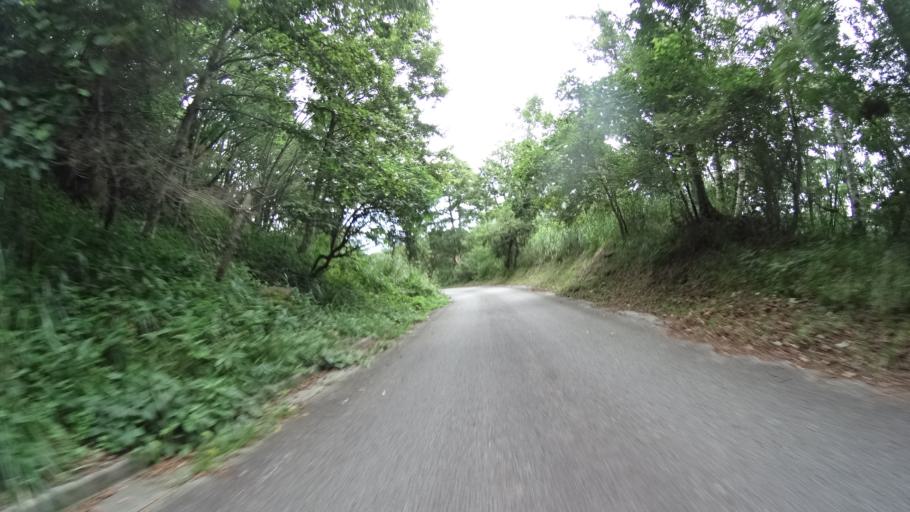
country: JP
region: Yamanashi
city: Kofu-shi
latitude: 35.8258
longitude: 138.5532
